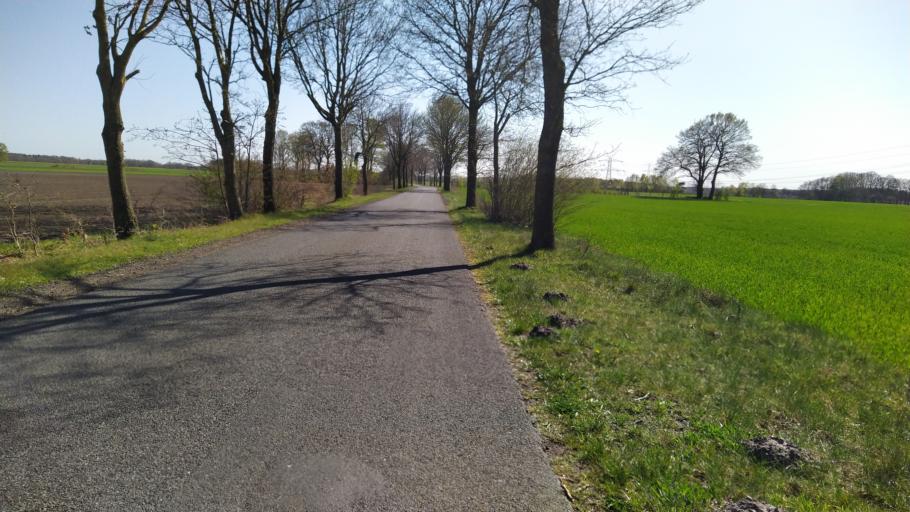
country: DE
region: Lower Saxony
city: Heeslingen
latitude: 53.3202
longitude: 9.3894
